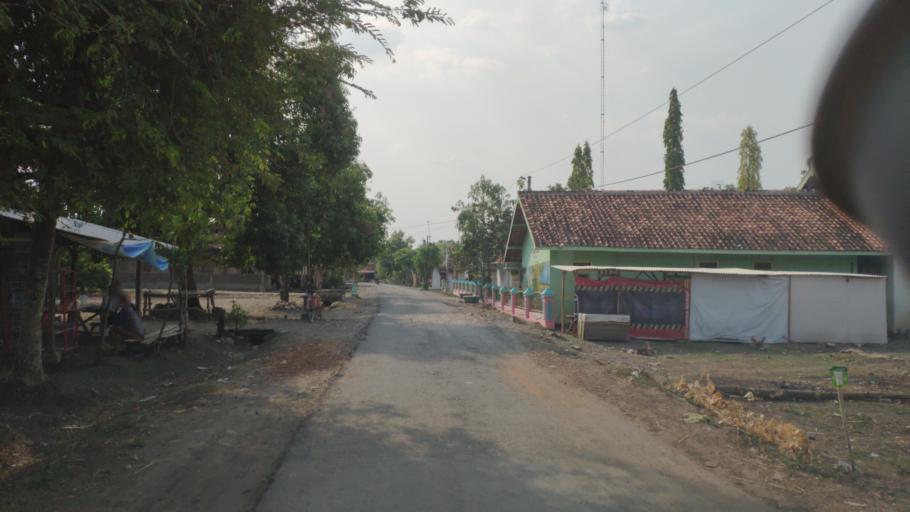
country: ID
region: Central Java
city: Randublatung
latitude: -7.2807
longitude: 111.2486
